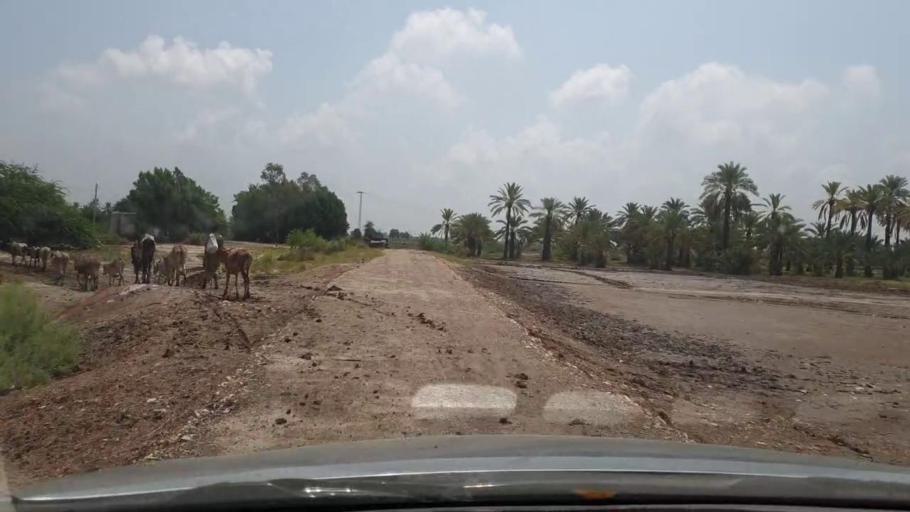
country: PK
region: Sindh
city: Khairpur
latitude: 27.4716
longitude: 68.6876
